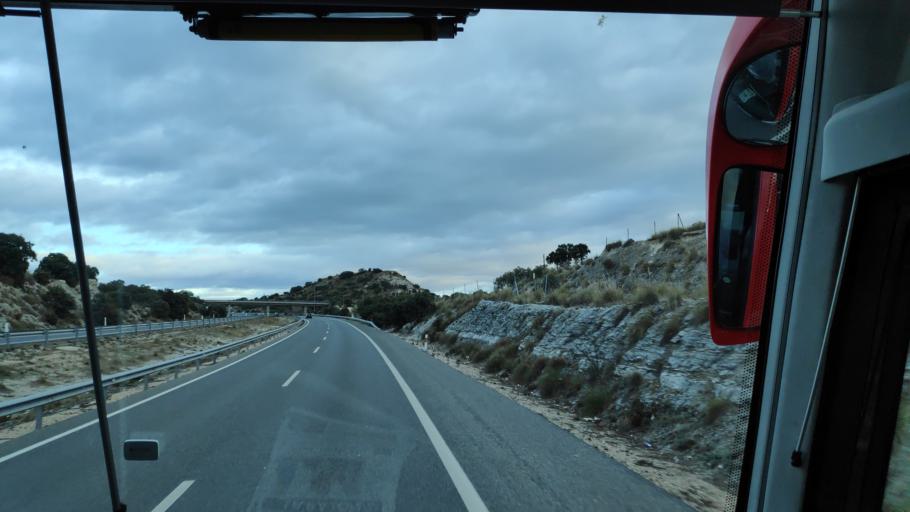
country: ES
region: Madrid
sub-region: Provincia de Madrid
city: Fuentiduena de Tajo
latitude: 40.1428
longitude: -3.2114
